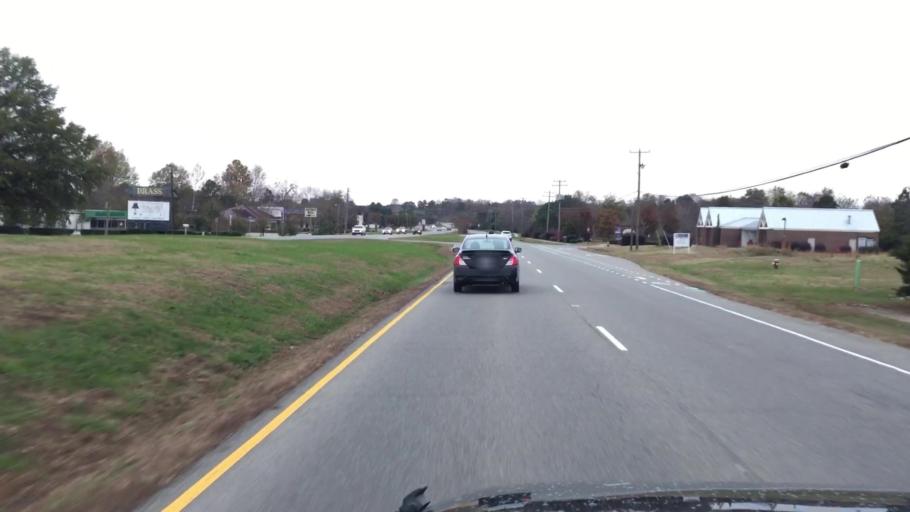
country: US
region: Virginia
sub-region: James City County
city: Williamsburg
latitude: 37.3546
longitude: -76.7638
